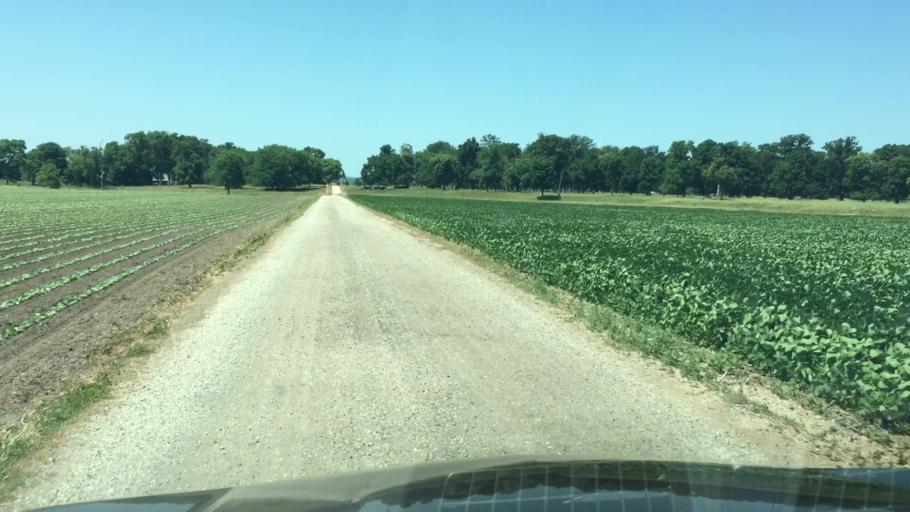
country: US
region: Wisconsin
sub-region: Fond du Lac County
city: Saint Peter
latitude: 43.9604
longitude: -88.3127
